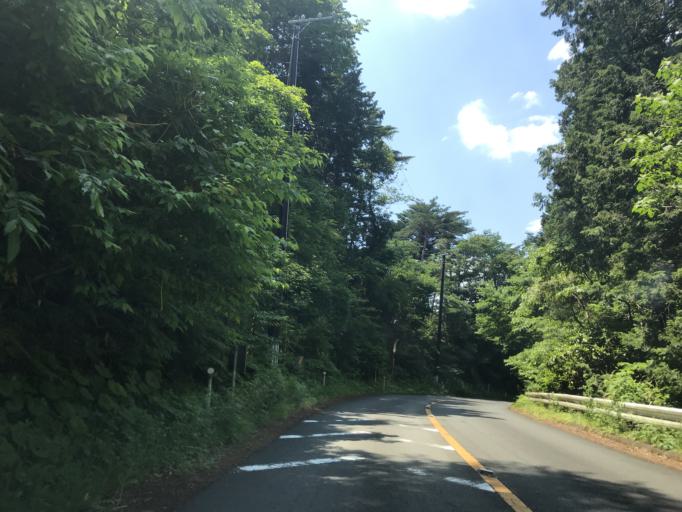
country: JP
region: Miyagi
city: Matsushima
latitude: 38.3592
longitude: 141.0552
